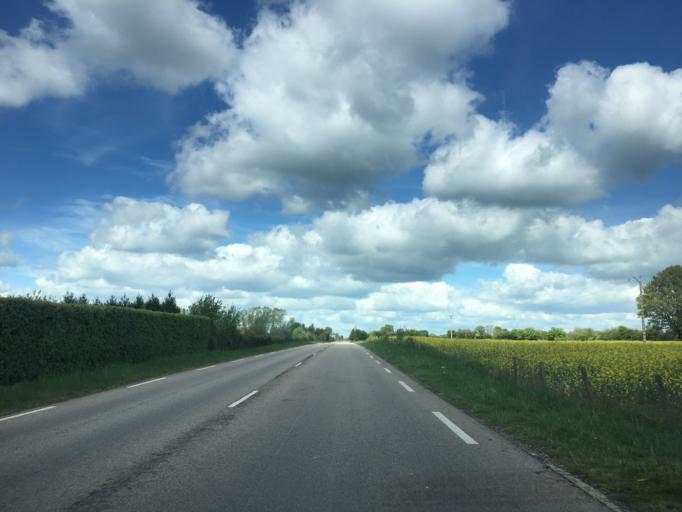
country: FR
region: Lower Normandy
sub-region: Departement de l'Orne
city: Rai
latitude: 48.8337
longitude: 0.5387
